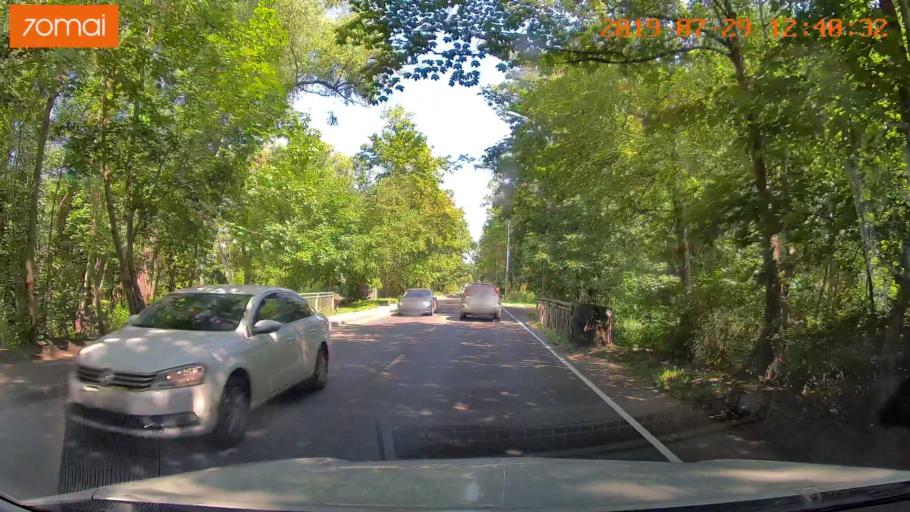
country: RU
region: Kaliningrad
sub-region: Gorod Kaliningrad
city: Kaliningrad
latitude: 54.6678
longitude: 20.5439
